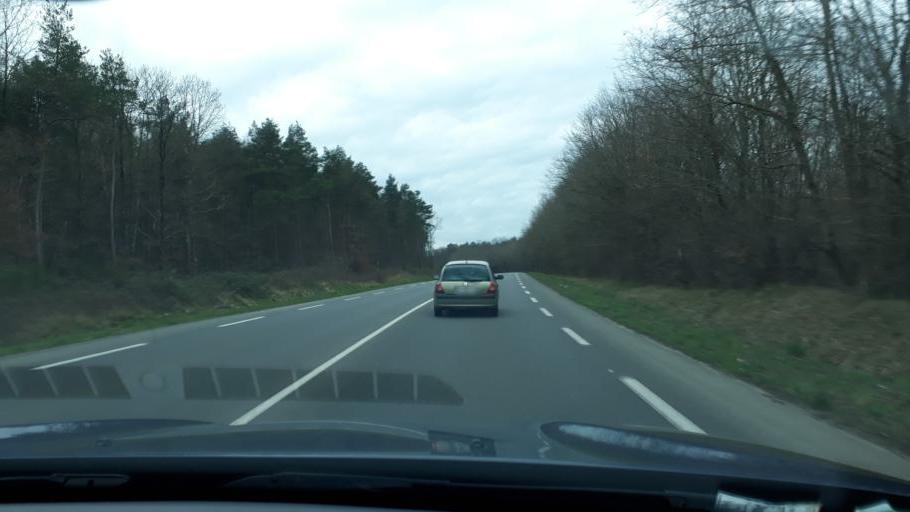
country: FR
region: Centre
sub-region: Departement du Loiret
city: Fleury-les-Aubrais
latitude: 47.9727
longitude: 1.9304
